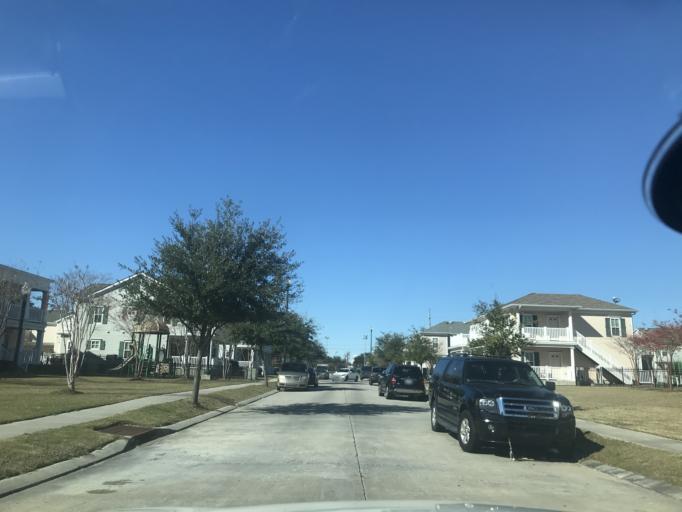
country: US
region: Louisiana
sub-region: Orleans Parish
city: New Orleans
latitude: 29.9529
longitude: -90.0943
